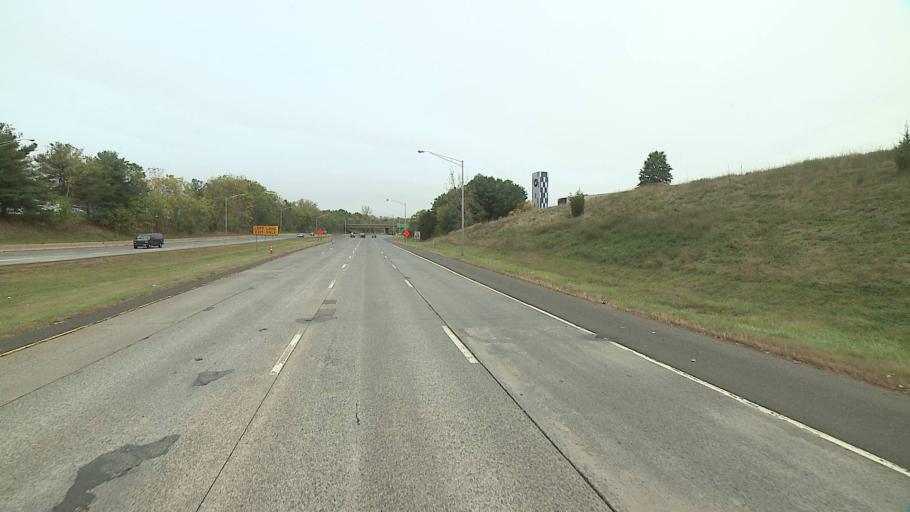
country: US
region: Connecticut
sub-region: Hartford County
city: New Britain
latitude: 41.6584
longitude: -72.7728
